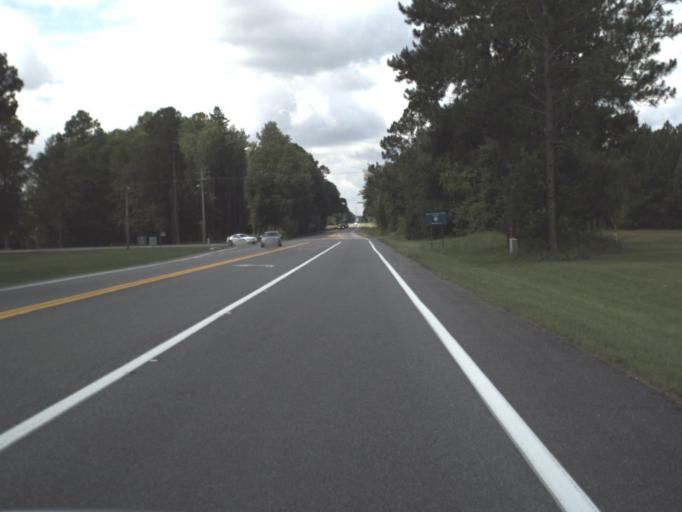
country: US
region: Florida
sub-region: Union County
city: Lake Butler
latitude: 30.0011
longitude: -82.3715
